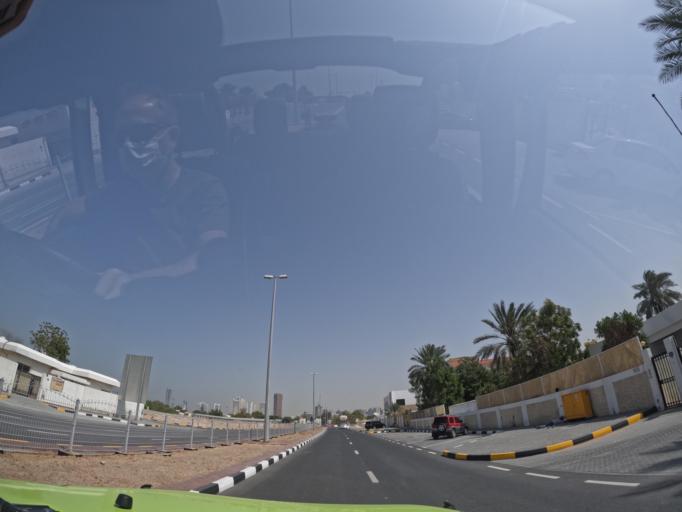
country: AE
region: Ajman
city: Ajman
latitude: 25.3823
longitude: 55.4201
